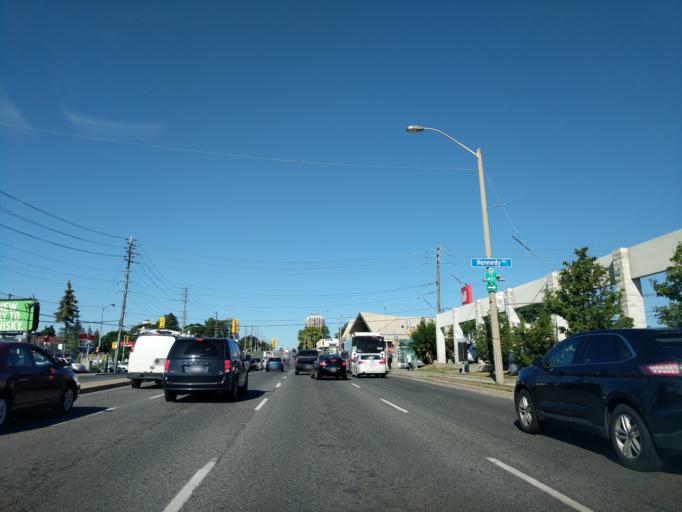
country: CA
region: Ontario
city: Scarborough
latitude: 43.7661
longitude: -79.2802
